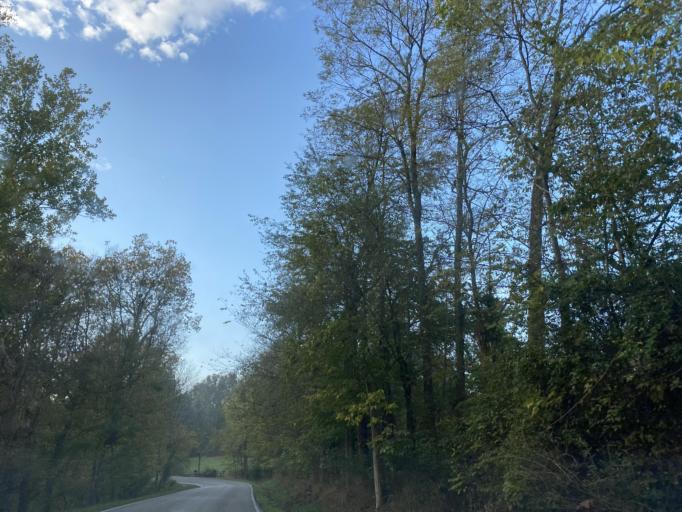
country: US
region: Kentucky
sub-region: Pendleton County
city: Falmouth
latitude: 38.7513
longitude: -84.3383
